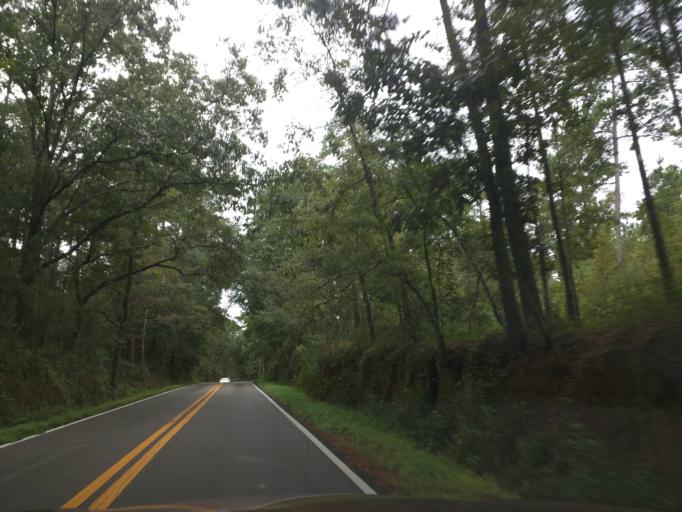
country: US
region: Florida
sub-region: Leon County
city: Tallahassee
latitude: 30.5153
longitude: -84.1341
